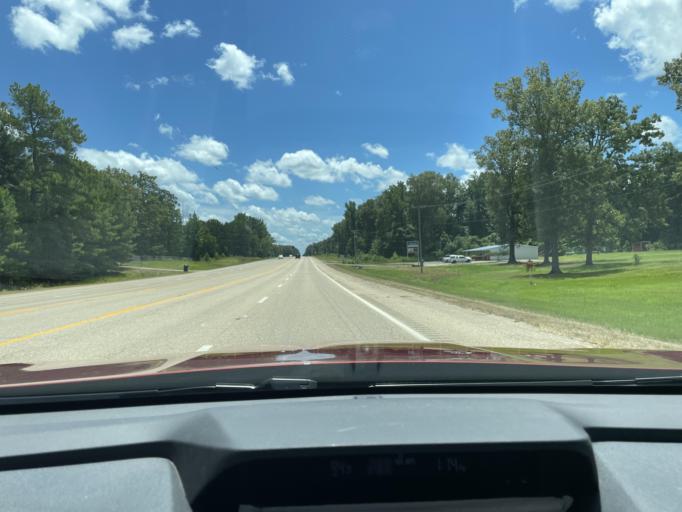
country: US
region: Arkansas
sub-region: Drew County
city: Monticello
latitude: 33.6648
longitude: -91.8037
